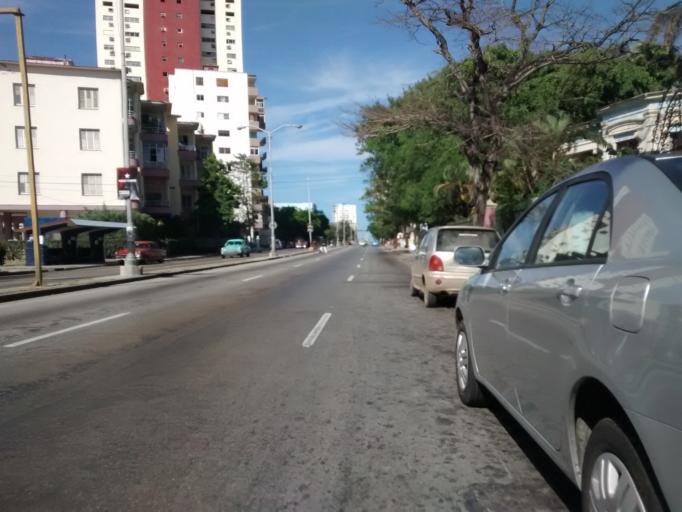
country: CU
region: La Habana
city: Havana
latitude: 23.1416
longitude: -82.3916
